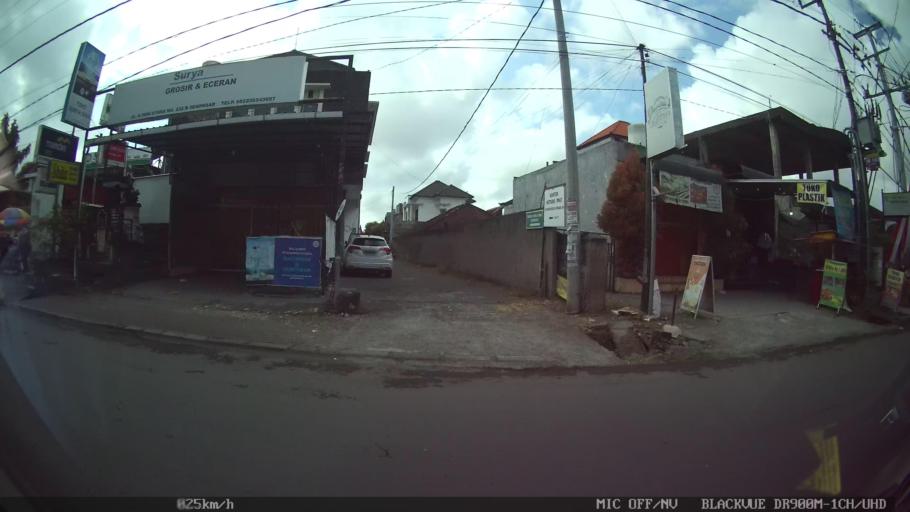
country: ID
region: Bali
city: Banjar Kertasari
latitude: -8.6250
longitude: 115.2086
